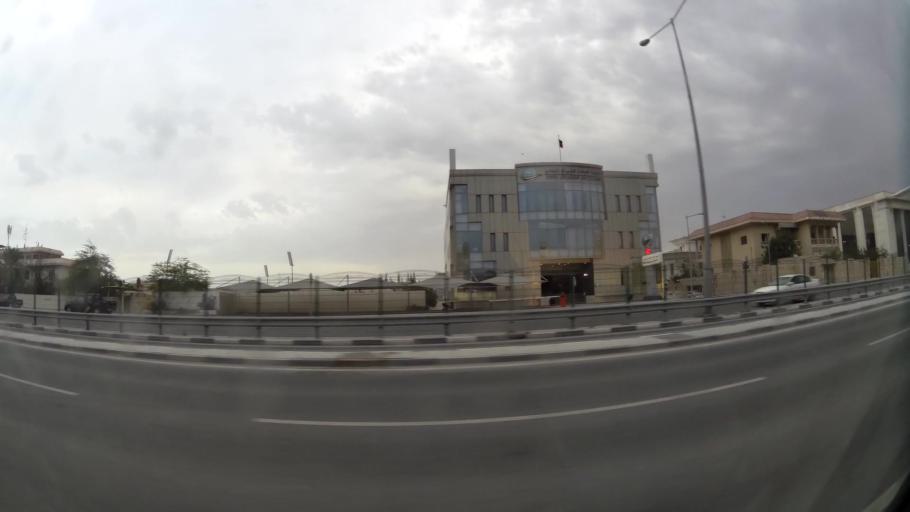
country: QA
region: Baladiyat ad Dawhah
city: Doha
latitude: 25.2644
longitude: 51.5201
